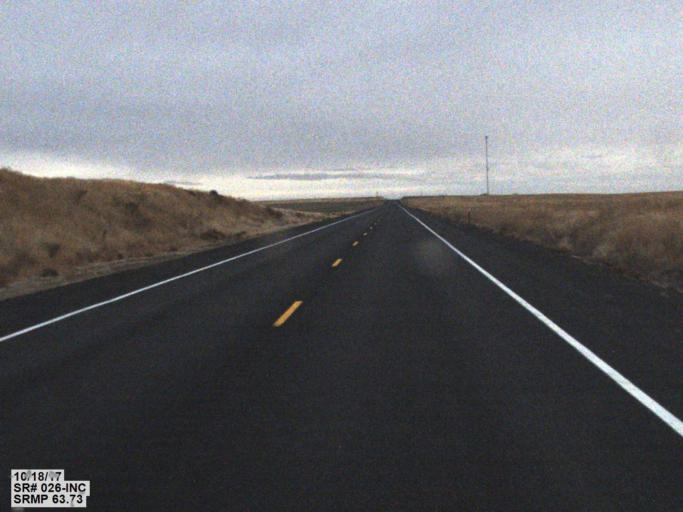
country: US
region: Washington
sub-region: Franklin County
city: Connell
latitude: 46.7944
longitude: -118.6920
